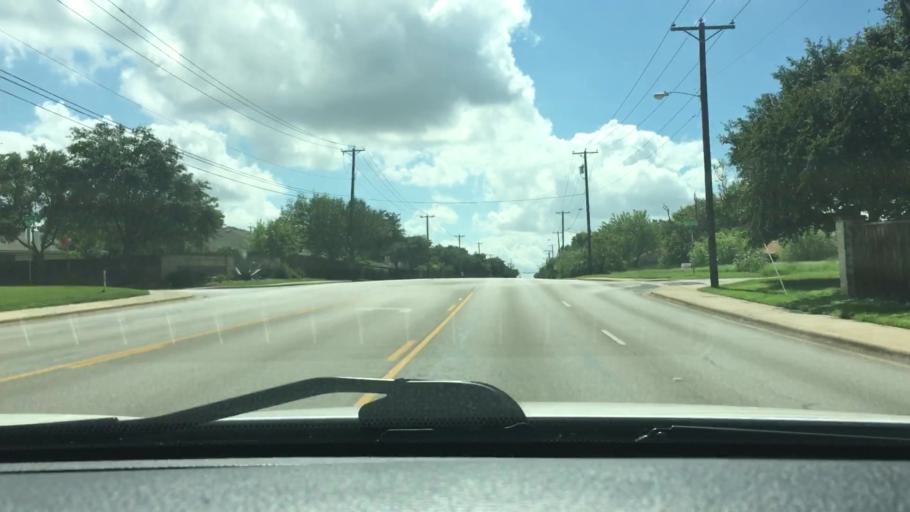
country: US
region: Texas
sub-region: Williamson County
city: Round Rock
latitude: 30.5366
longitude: -97.6681
